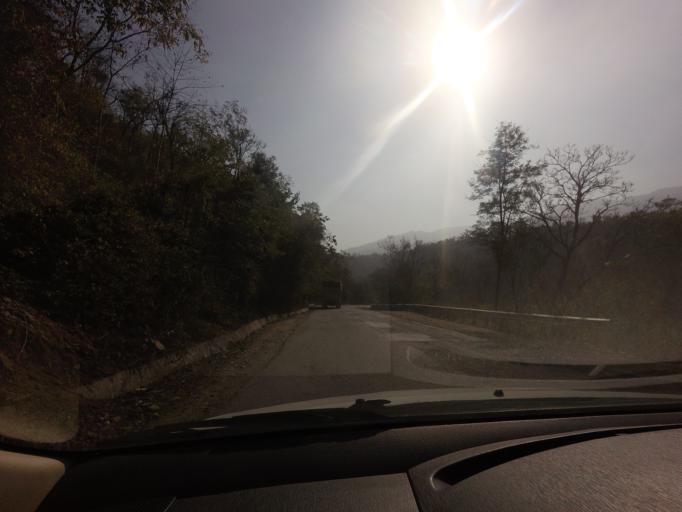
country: IN
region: Himachal Pradesh
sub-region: Solan
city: Arki
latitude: 31.2430
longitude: 76.9126
